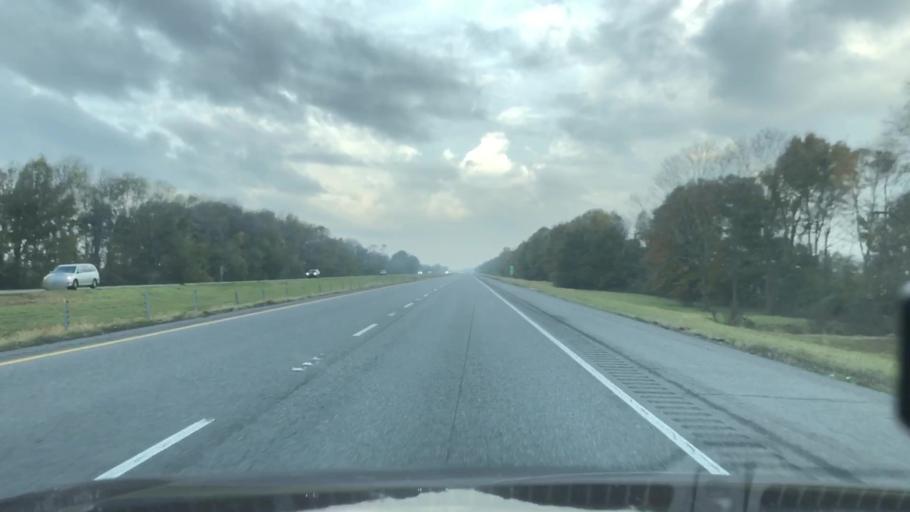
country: US
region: Louisiana
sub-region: Madison Parish
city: Tallulah
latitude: 32.4097
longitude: -91.2489
